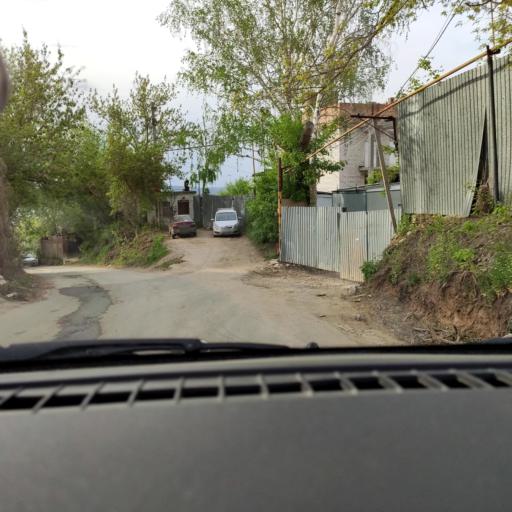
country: RU
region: Samara
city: Samara
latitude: 53.2800
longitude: 50.1896
